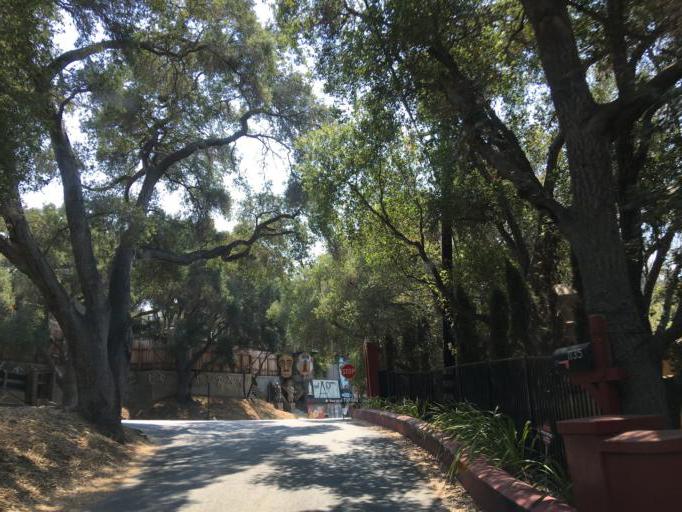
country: US
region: California
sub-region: Los Angeles County
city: Topanga
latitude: 34.1050
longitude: -118.5922
